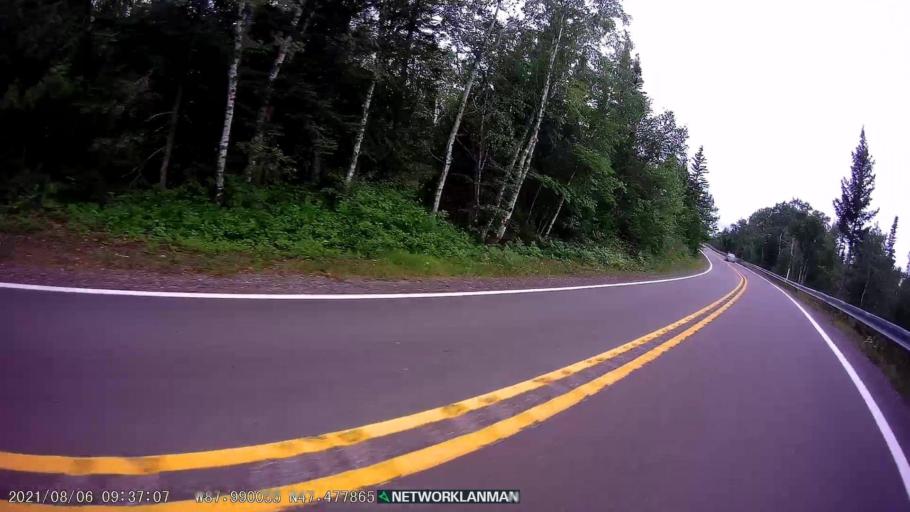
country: US
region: Michigan
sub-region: Keweenaw County
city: Eagle River
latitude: 47.4781
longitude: -87.9909
